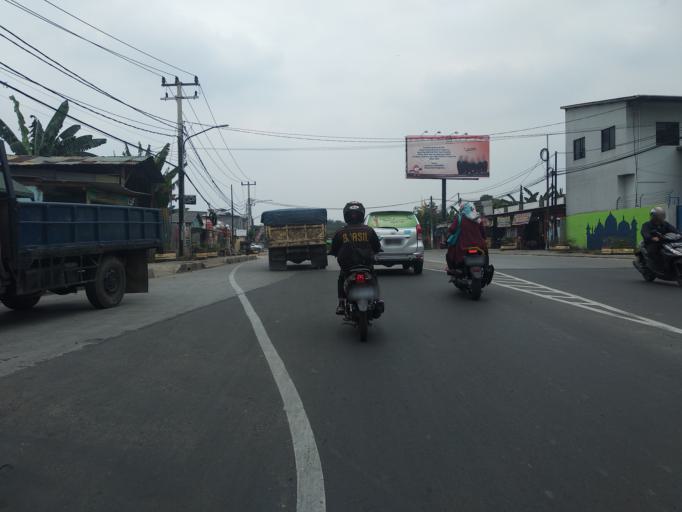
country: ID
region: West Java
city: Ciputat
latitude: -6.1964
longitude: 106.6776
